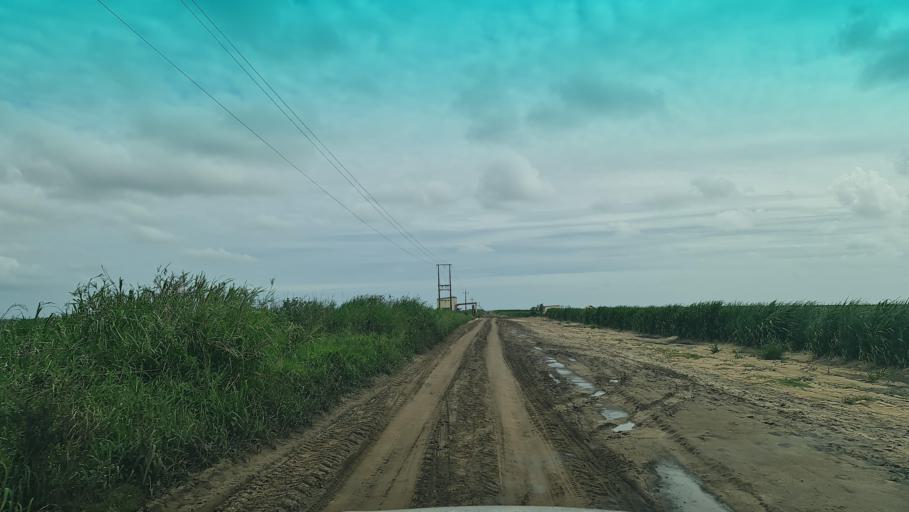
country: MZ
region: Maputo
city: Manhica
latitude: -25.4527
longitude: 32.8390
